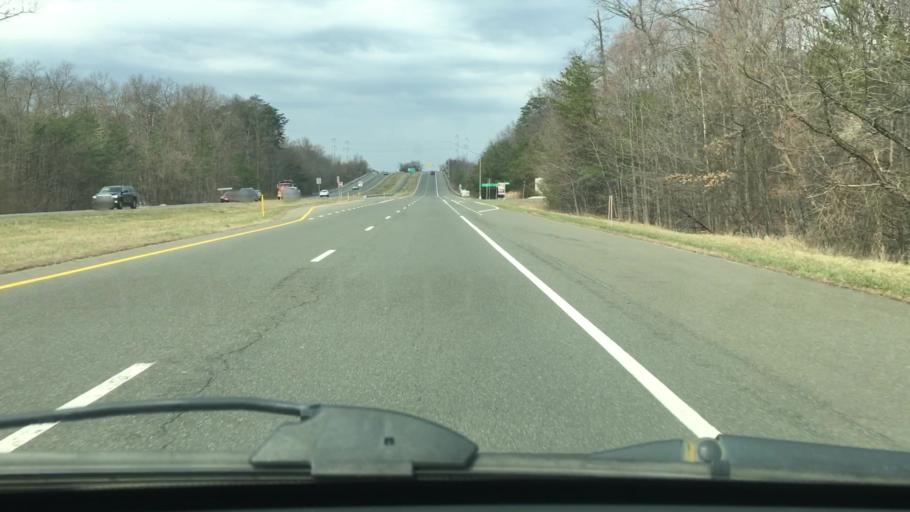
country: US
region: Maryland
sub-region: Prince George's County
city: Glenn Dale
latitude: 38.9843
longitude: -76.8110
